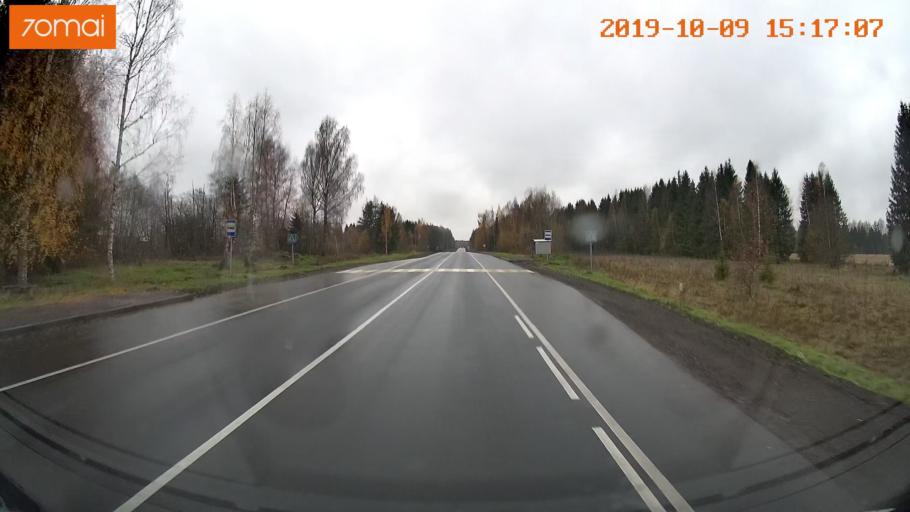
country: RU
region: Kostroma
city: Susanino
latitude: 58.1026
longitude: 41.5839
